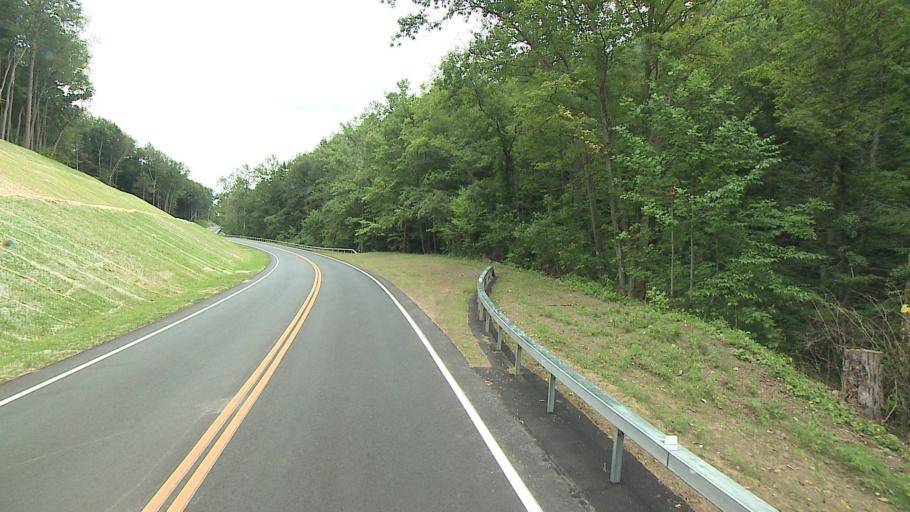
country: US
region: Connecticut
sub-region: Fairfield County
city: Newtown
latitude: 41.4897
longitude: -73.3516
